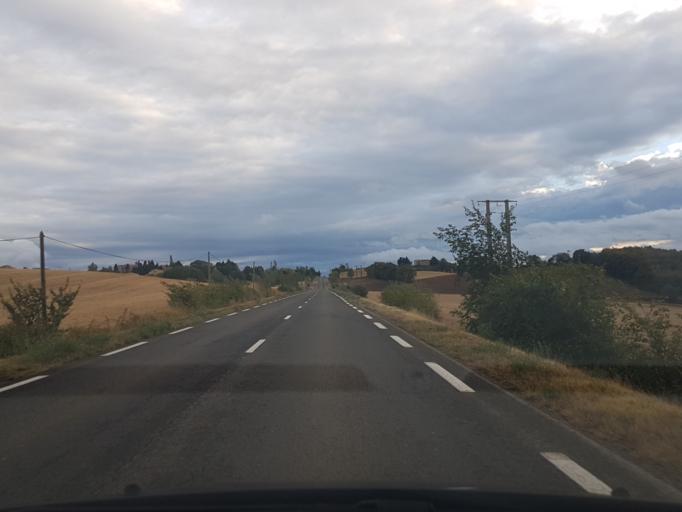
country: FR
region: Midi-Pyrenees
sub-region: Departement de l'Ariege
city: Mirepoix
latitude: 43.1346
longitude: 1.9520
